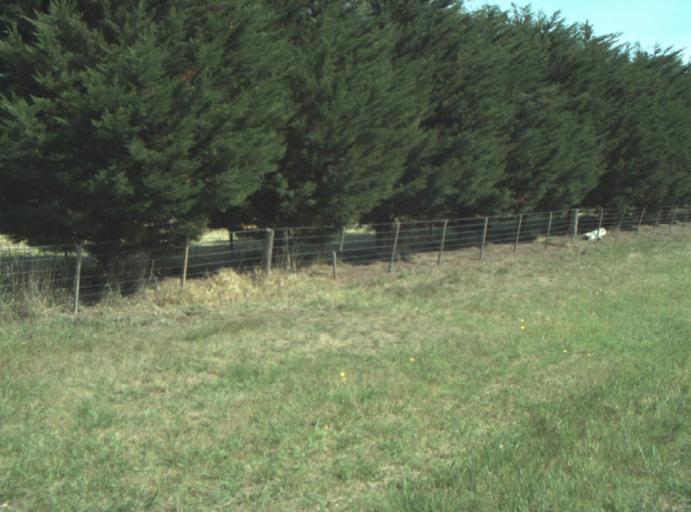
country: AU
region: Victoria
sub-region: Greater Geelong
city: Leopold
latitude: -38.2033
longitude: 144.5087
